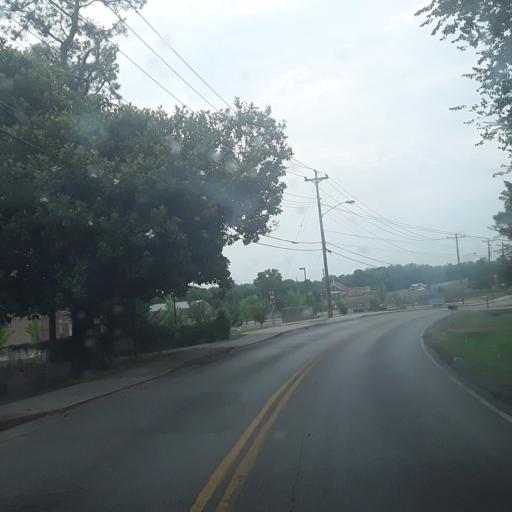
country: US
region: Tennessee
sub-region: Davidson County
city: Oak Hill
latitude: 36.0612
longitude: -86.7211
